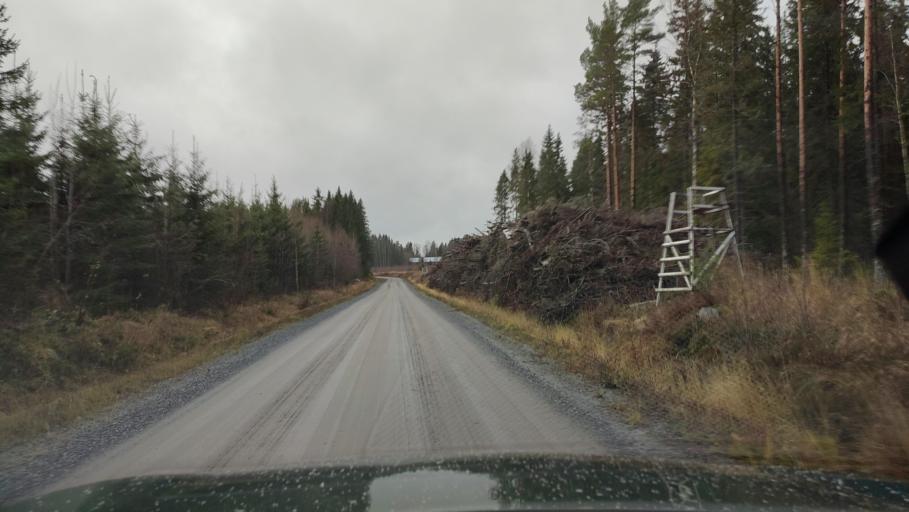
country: FI
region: Ostrobothnia
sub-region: Sydosterbotten
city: Naerpes
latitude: 62.4529
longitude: 21.4669
